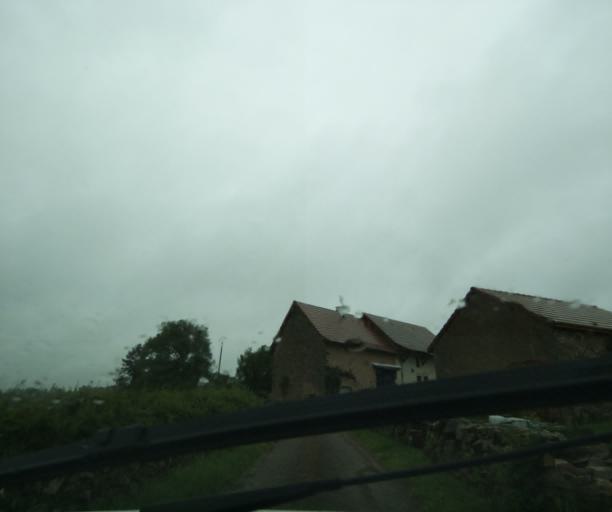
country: FR
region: Bourgogne
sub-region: Departement de Saone-et-Loire
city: Charolles
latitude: 46.3857
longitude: 4.3276
